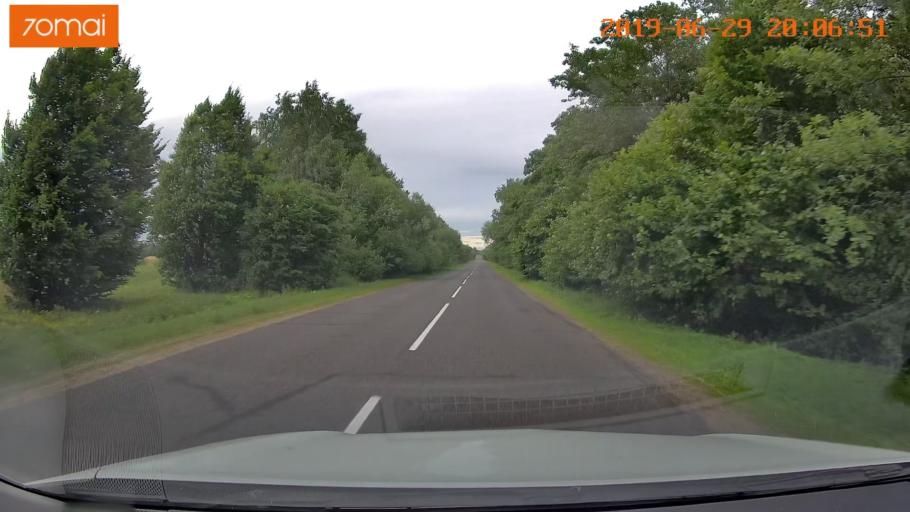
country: BY
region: Brest
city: Lahishyn
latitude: 52.3397
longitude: 26.0220
